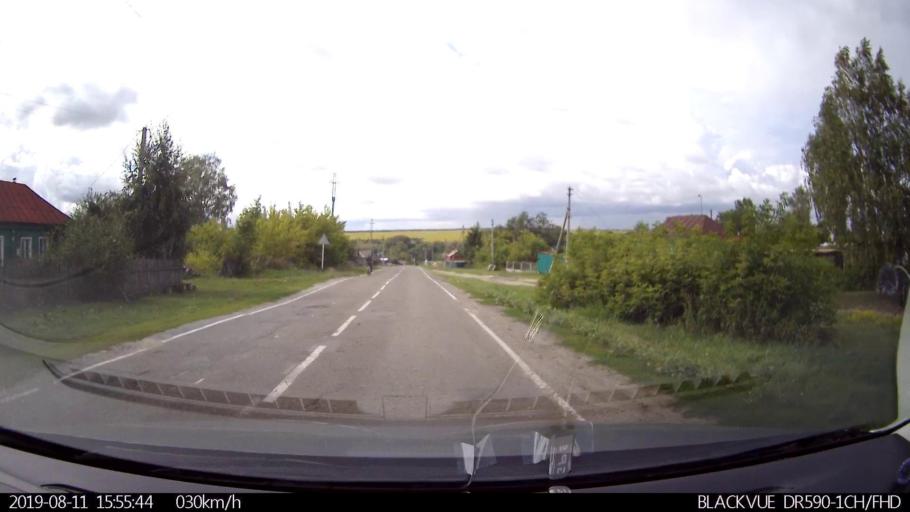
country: RU
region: Ulyanovsk
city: Ignatovka
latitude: 53.9462
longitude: 47.6527
